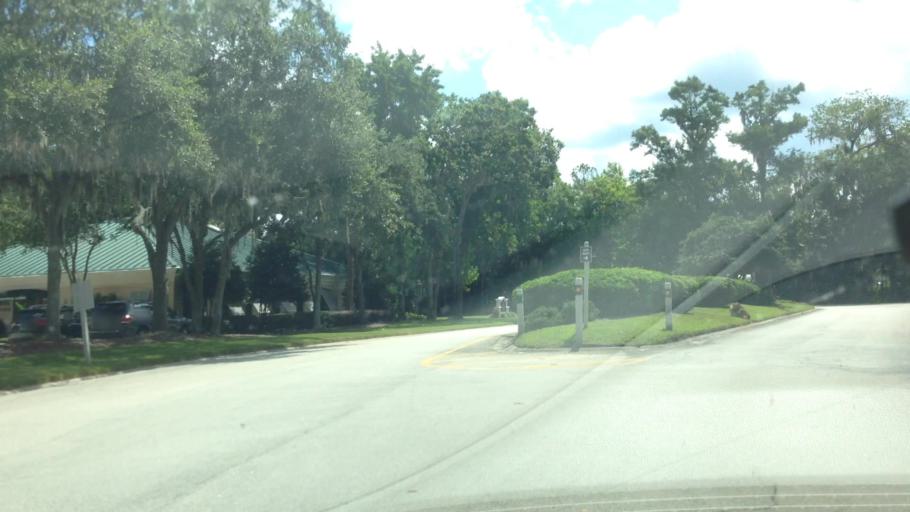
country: US
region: Florida
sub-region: Saint Johns County
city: Ponte Vedra Beach
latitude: 30.2537
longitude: -81.4015
